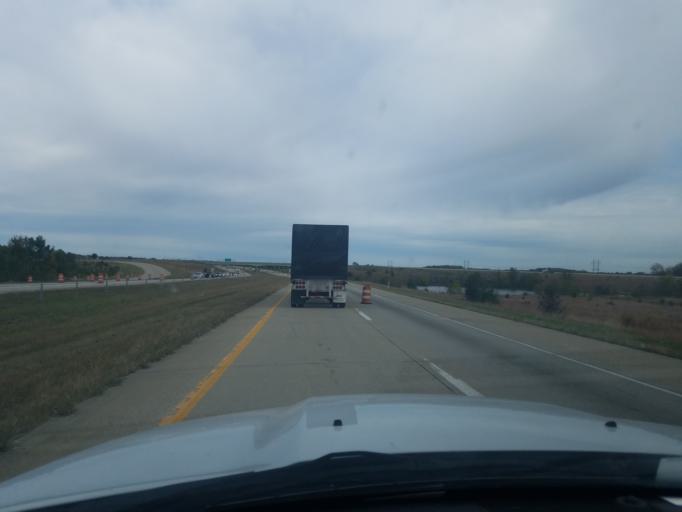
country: US
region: Indiana
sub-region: Vanderburgh County
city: Darmstadt
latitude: 38.1308
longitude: -87.4743
